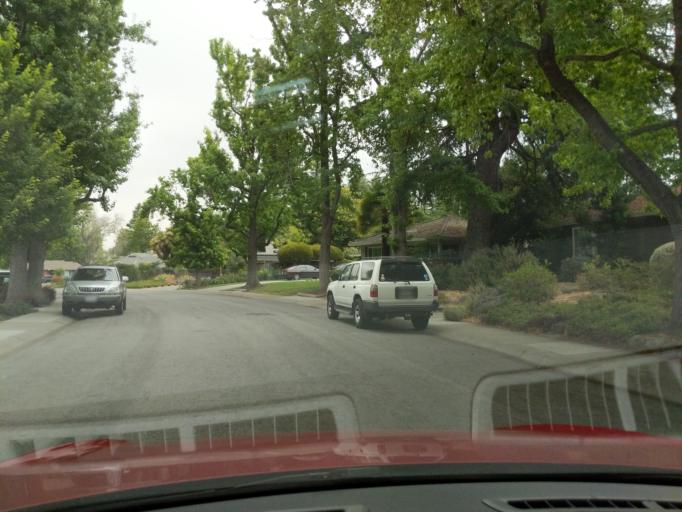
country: US
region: California
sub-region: San Mateo County
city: Menlo Park
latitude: 37.4510
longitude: -122.1683
